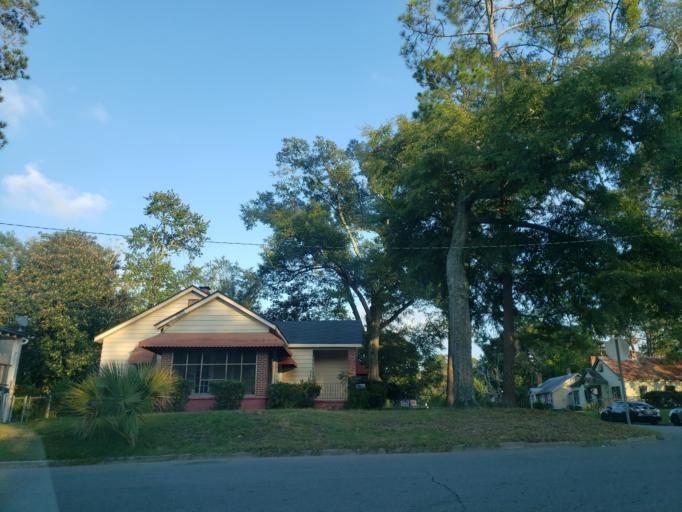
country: US
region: Georgia
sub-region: Chatham County
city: Thunderbolt
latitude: 32.0532
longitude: -81.0776
